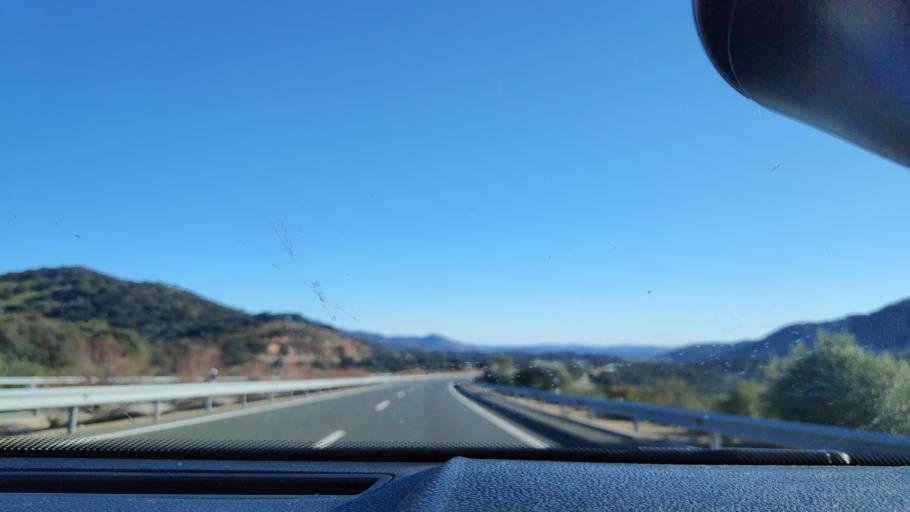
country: ES
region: Extremadura
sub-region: Provincia de Badajoz
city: Monesterio
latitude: 38.0693
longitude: -6.2473
